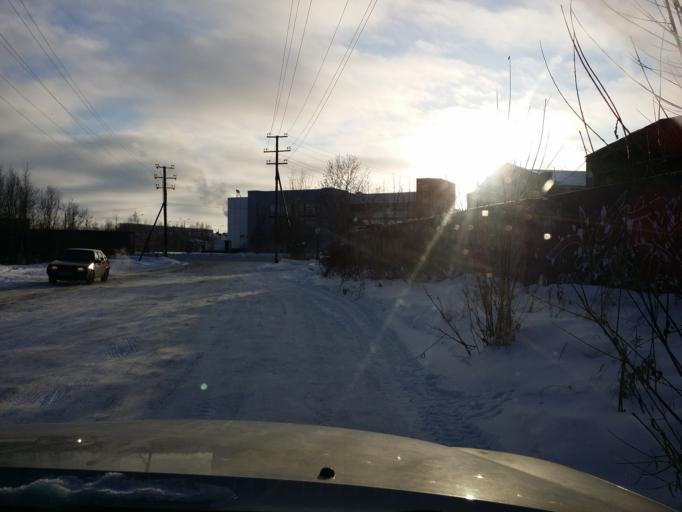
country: RU
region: Khanty-Mansiyskiy Avtonomnyy Okrug
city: Megion
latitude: 61.0421
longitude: 76.1027
